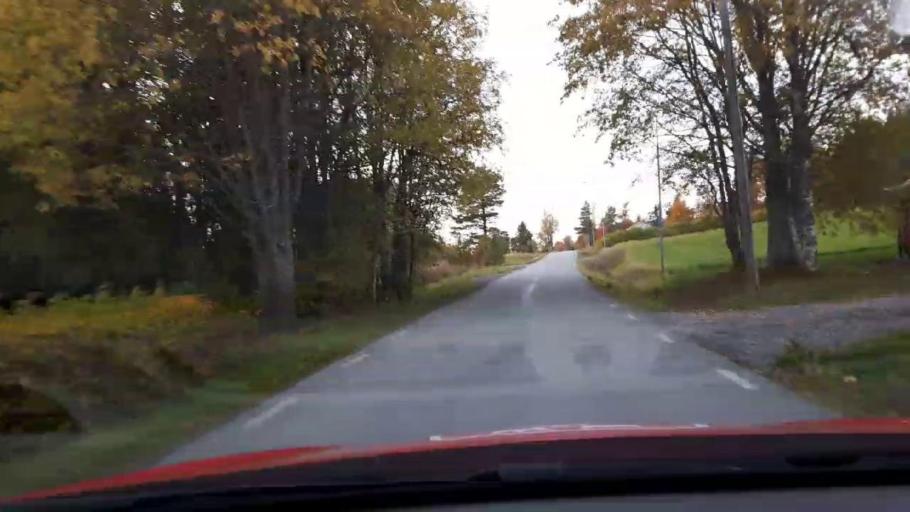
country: SE
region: Jaemtland
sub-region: Krokoms Kommun
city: Krokom
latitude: 63.3640
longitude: 14.4949
